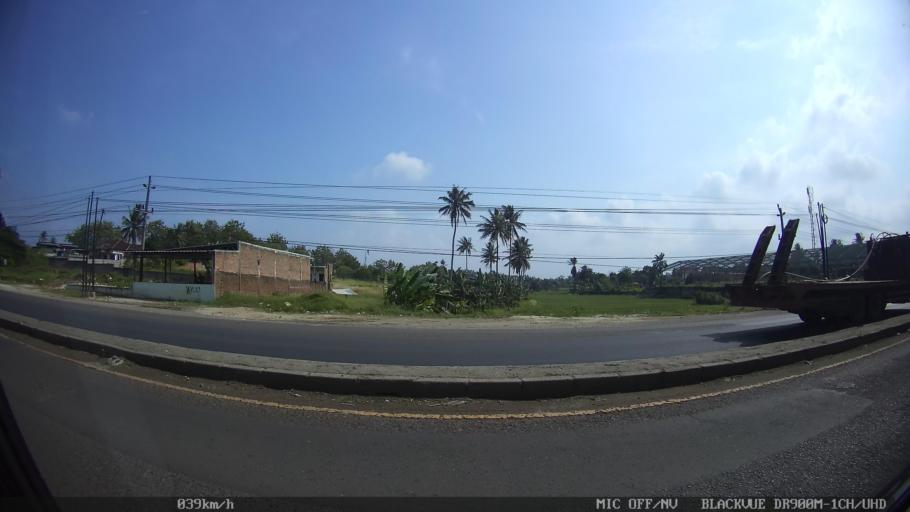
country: ID
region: Lampung
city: Kedaton
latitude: -5.3579
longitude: 105.2506
